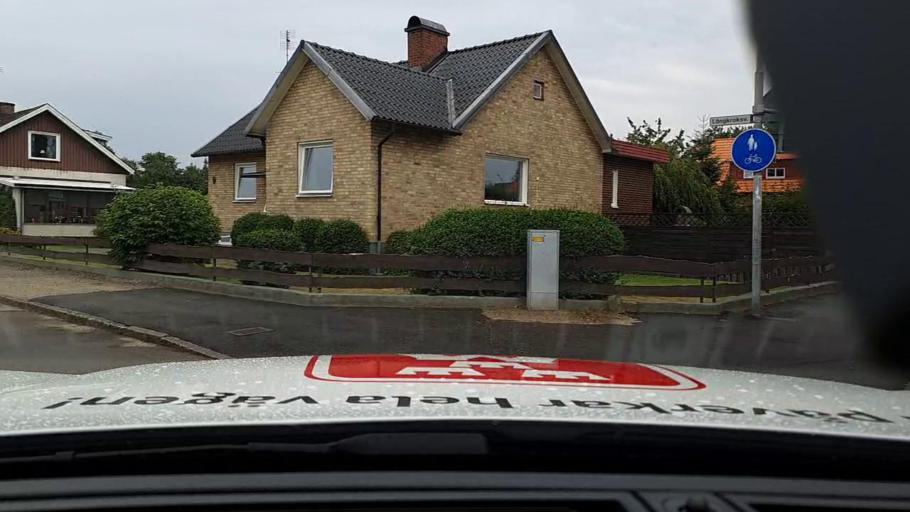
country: SE
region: Skane
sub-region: Hassleholms Kommun
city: Hassleholm
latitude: 56.1646
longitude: 13.7735
